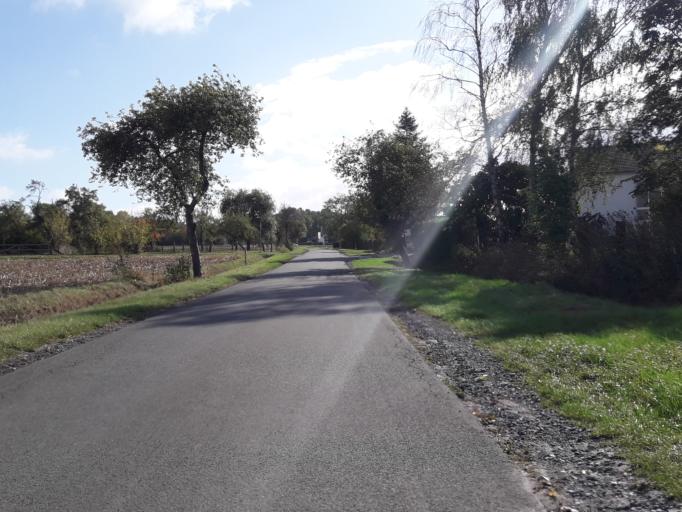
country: DE
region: North Rhine-Westphalia
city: Bad Lippspringe
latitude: 51.7408
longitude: 8.8064
